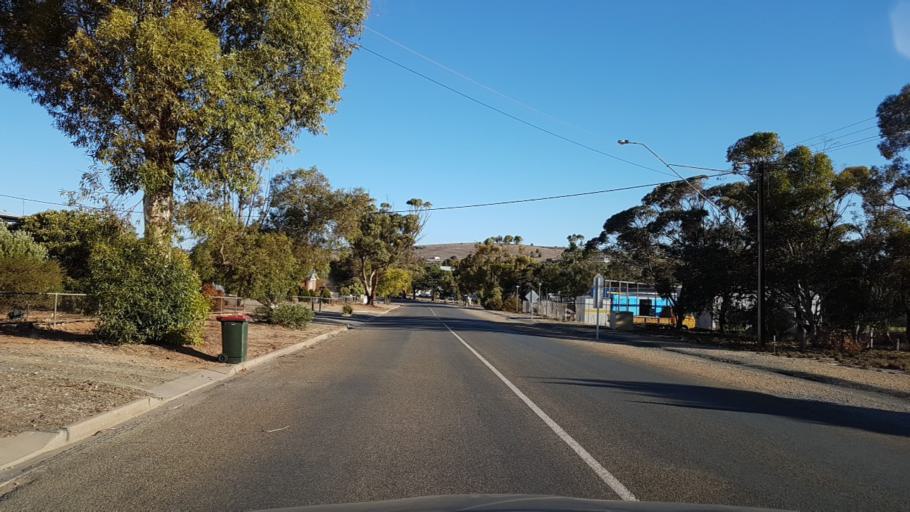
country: AU
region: South Australia
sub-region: Clare and Gilbert Valleys
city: Clare
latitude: -33.6780
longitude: 138.9409
